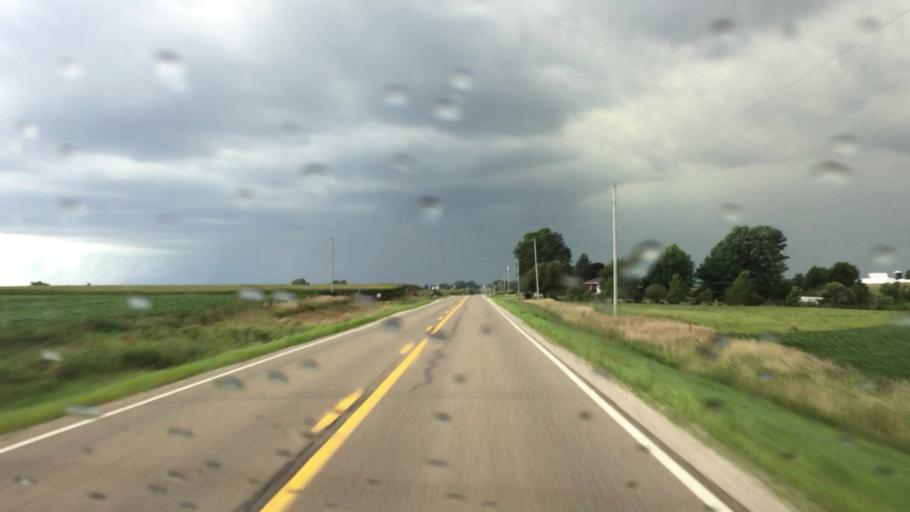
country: US
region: Iowa
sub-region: Henry County
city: Mount Pleasant
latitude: 40.7843
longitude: -91.5228
